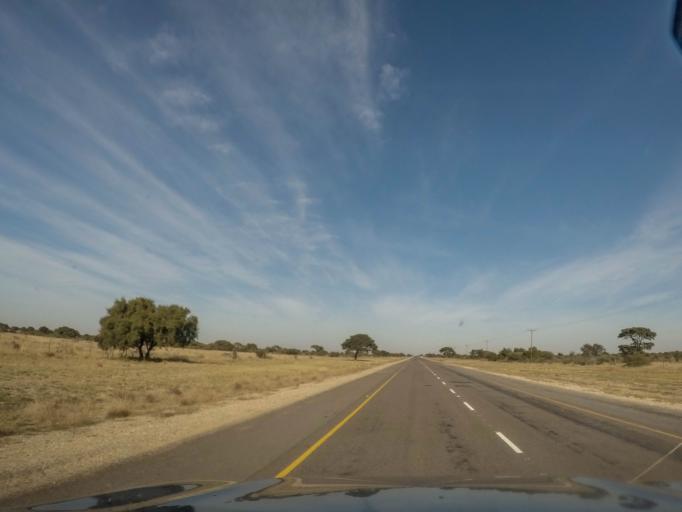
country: BW
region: South East
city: Janeng
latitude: -25.5550
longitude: 25.3161
